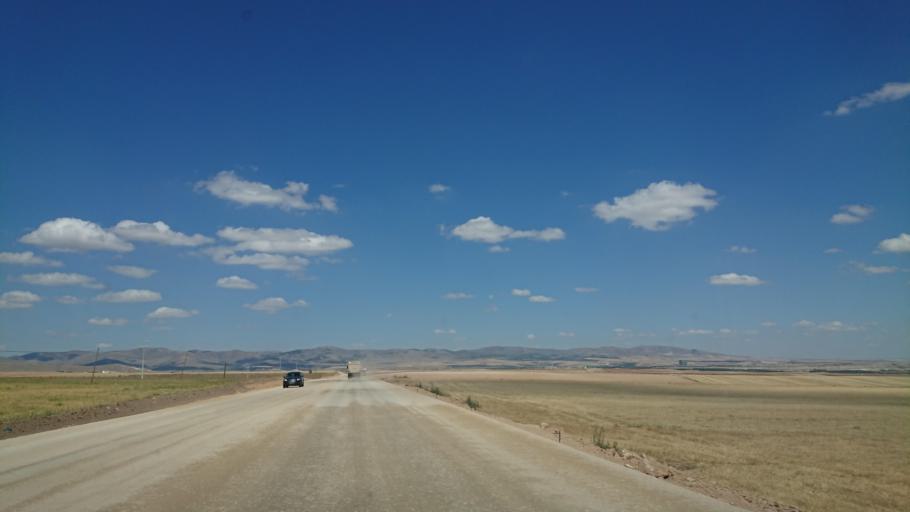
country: TR
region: Kirsehir
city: Kirsehir
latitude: 39.1390
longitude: 34.0645
